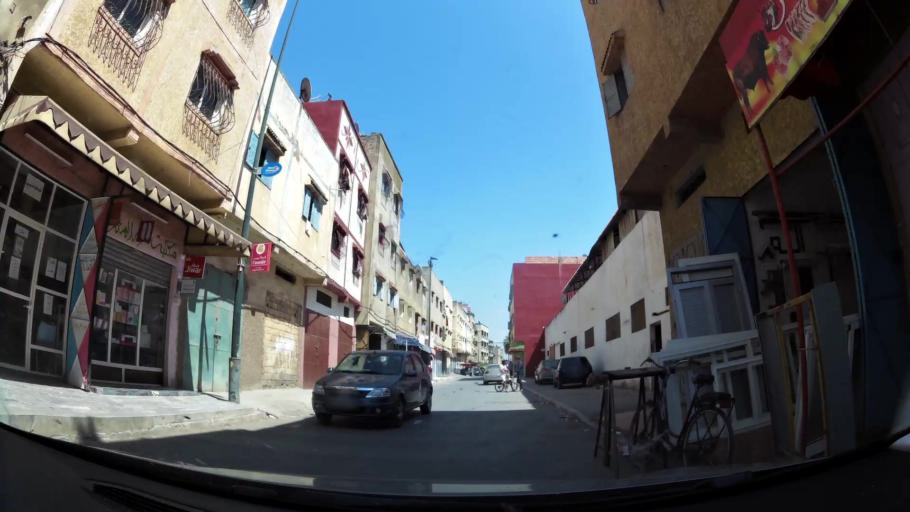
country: MA
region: Rabat-Sale-Zemmour-Zaer
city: Sale
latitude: 34.0668
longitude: -6.7783
